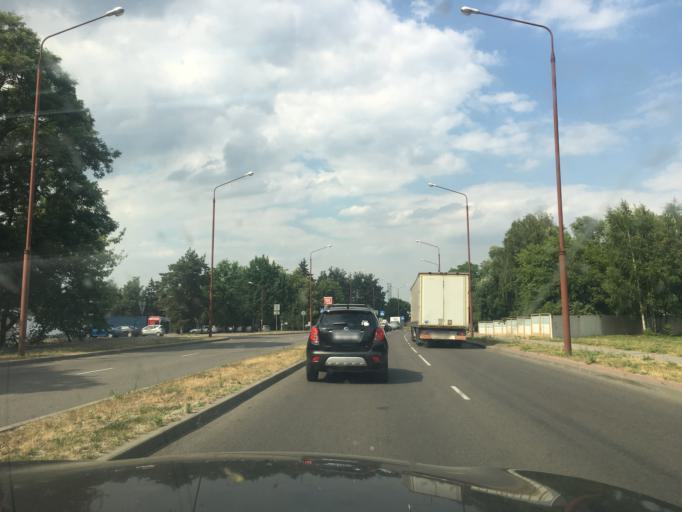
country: BY
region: Brest
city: Brest
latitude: 52.1371
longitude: 23.6759
